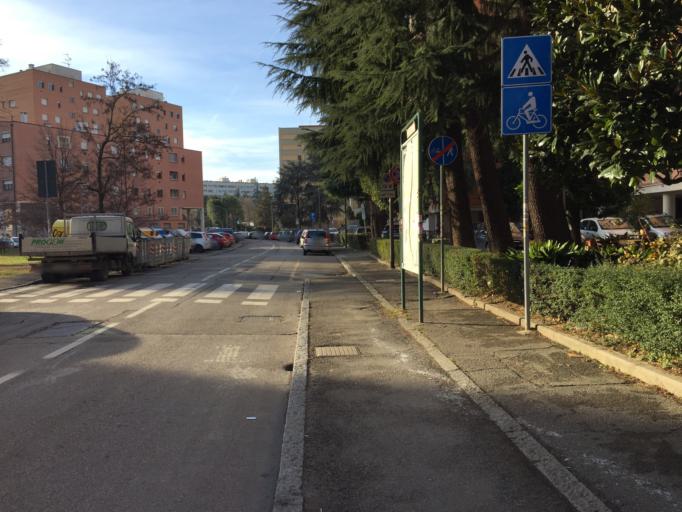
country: IT
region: Emilia-Romagna
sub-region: Provincia di Bologna
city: Casalecchio di Reno
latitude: 44.4951
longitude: 11.2926
